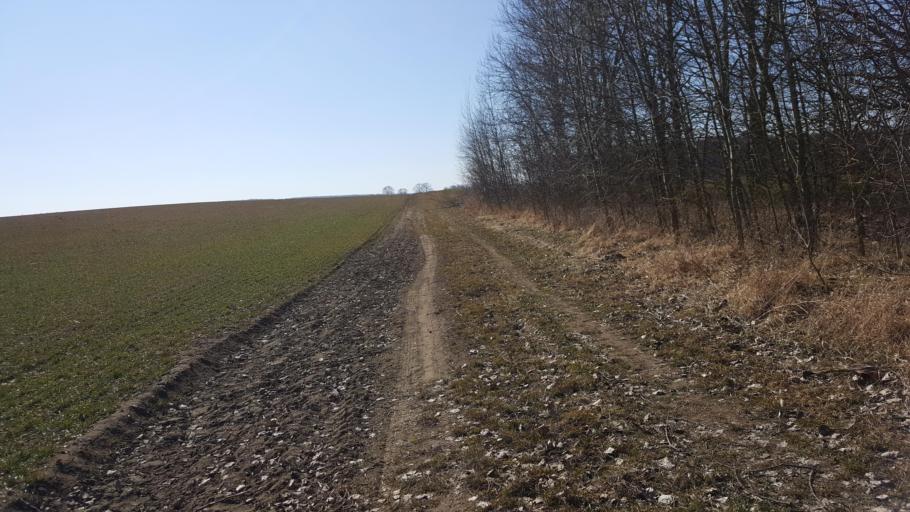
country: BY
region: Brest
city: Kamyanyets
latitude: 52.3691
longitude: 23.7750
